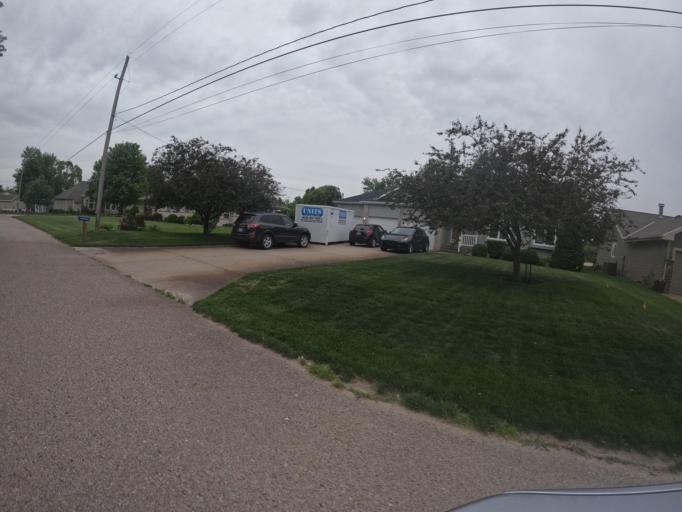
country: US
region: Nebraska
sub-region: Sarpy County
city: Offutt Air Force Base
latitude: 41.0562
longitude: -95.9564
